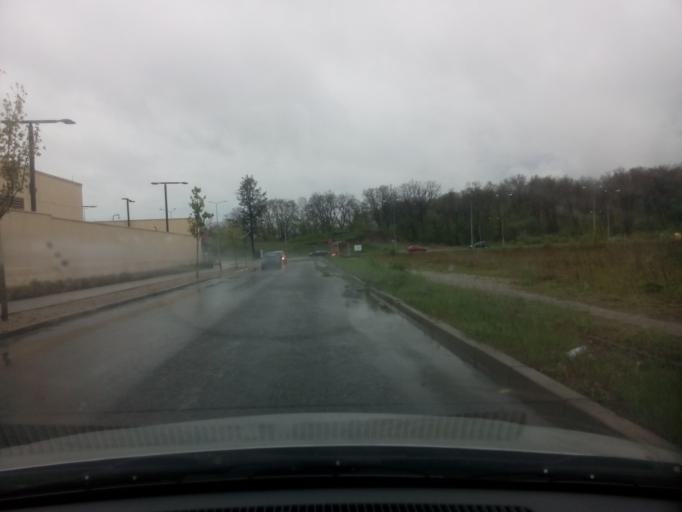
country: RO
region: Ilfov
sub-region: Comuna Otopeni
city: Otopeni
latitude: 44.5147
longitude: 26.0880
